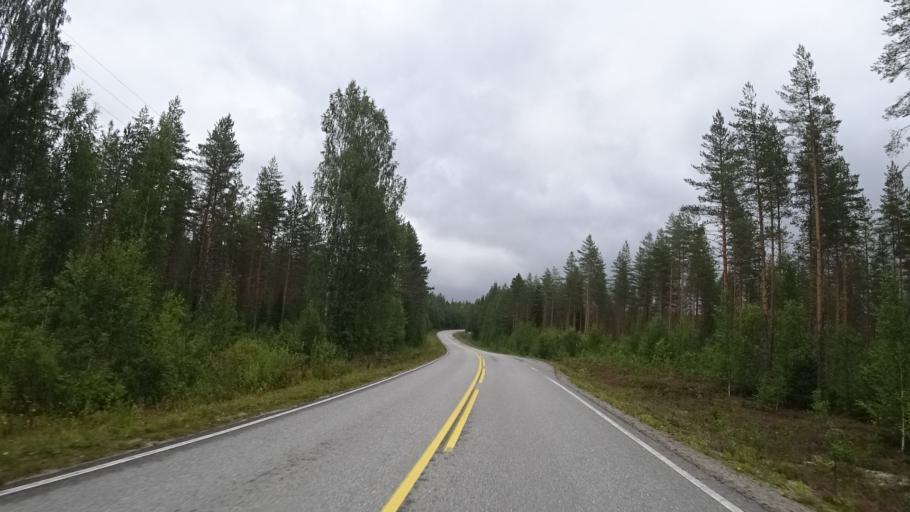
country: FI
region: North Karelia
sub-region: Joensuu
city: Ilomantsi
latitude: 63.2521
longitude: 30.7330
